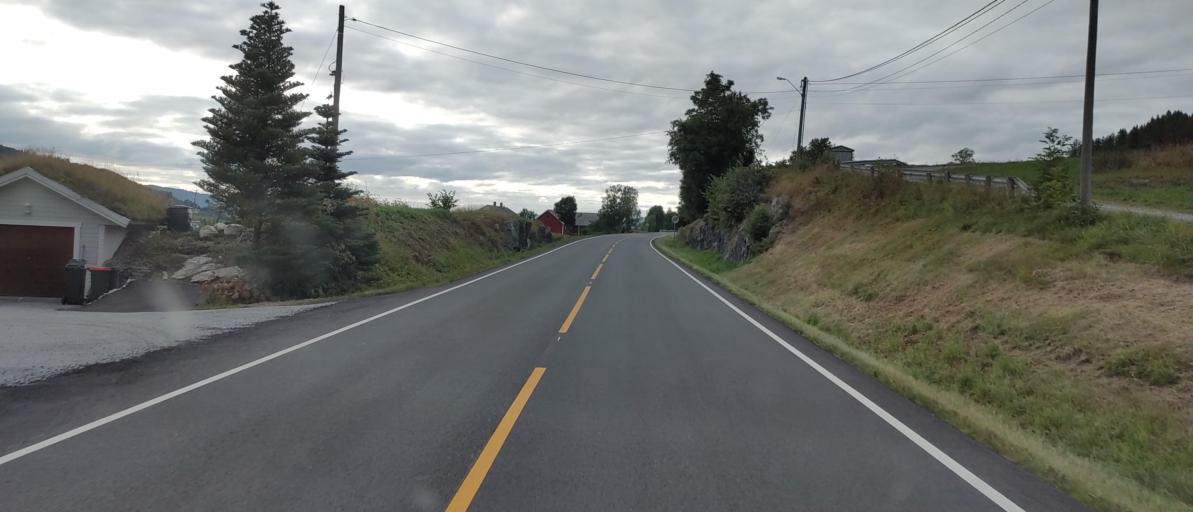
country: NO
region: More og Romsdal
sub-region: Molde
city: Hjelset
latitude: 62.6344
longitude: 7.5156
